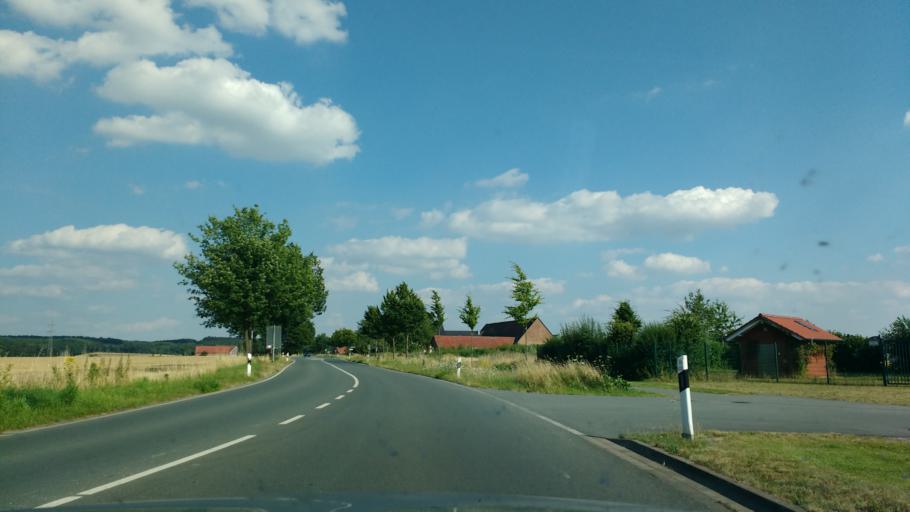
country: DE
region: North Rhine-Westphalia
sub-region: Regierungsbezirk Detmold
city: Salzkotten
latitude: 51.6697
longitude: 8.6250
